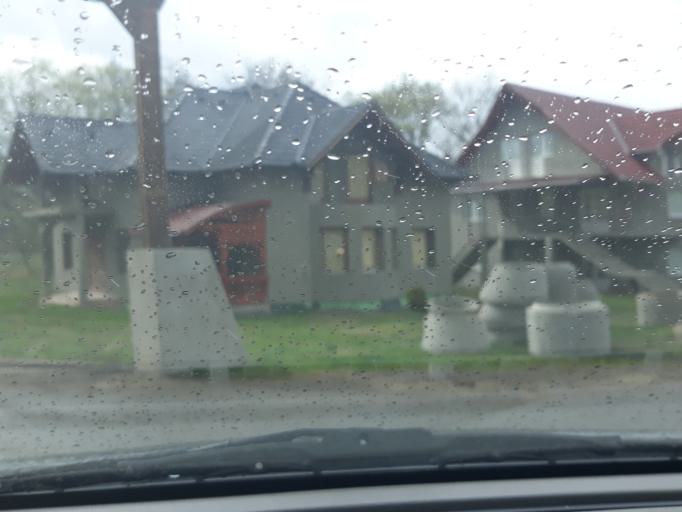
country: RO
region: Harghita
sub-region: Comuna Corund
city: Corund
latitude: 46.4859
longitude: 25.1697
